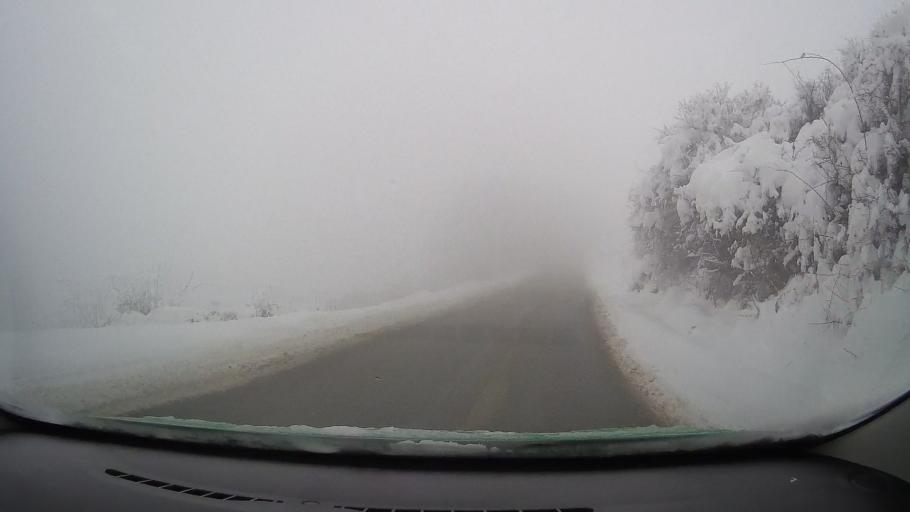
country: RO
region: Sibiu
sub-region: Comuna Poiana Sibiului
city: Poiana Sibiului
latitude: 45.8085
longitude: 23.7458
